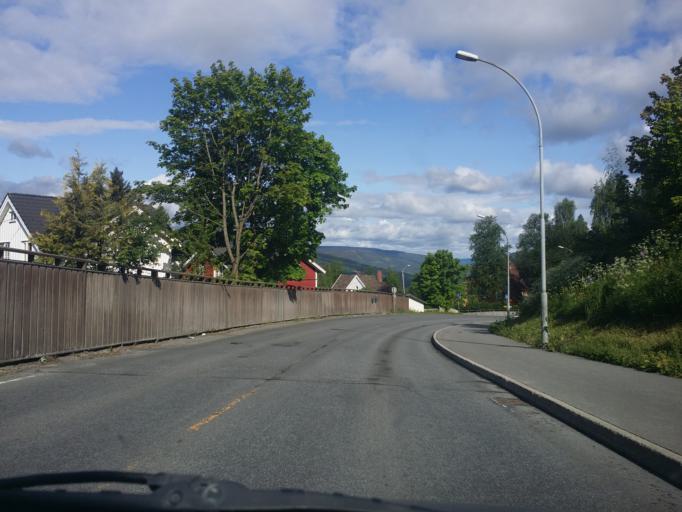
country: NO
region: Oppland
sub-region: Lillehammer
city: Lillehammer
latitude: 61.1083
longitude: 10.4748
